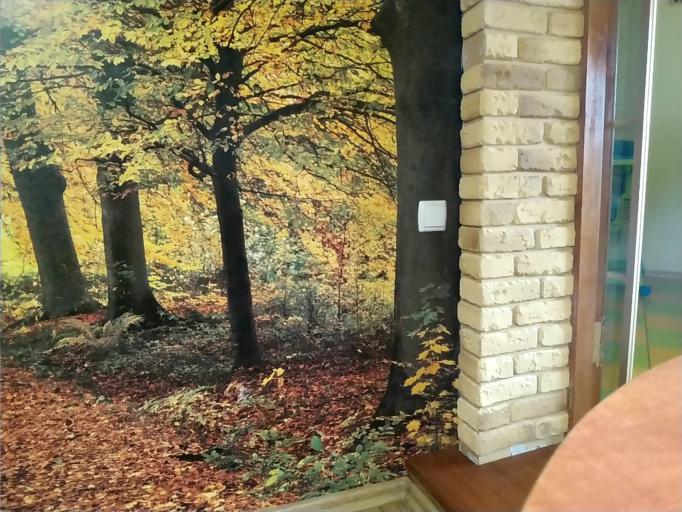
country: RU
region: Smolensk
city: Dorogobuzh
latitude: 54.8787
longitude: 33.3118
